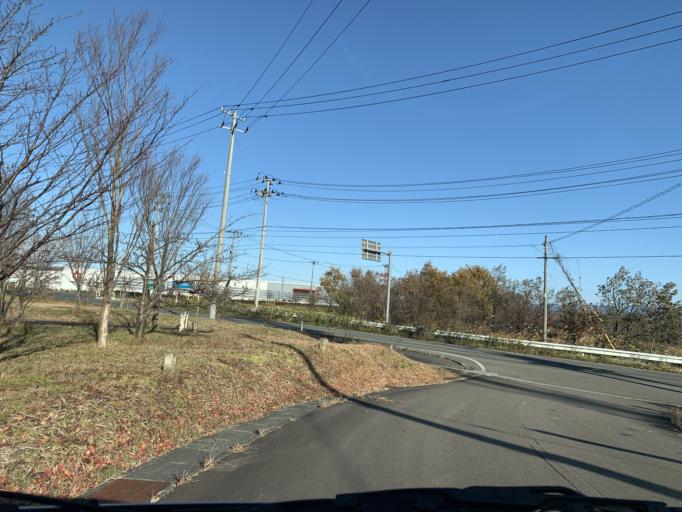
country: JP
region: Iwate
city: Kitakami
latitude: 39.2383
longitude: 141.0835
